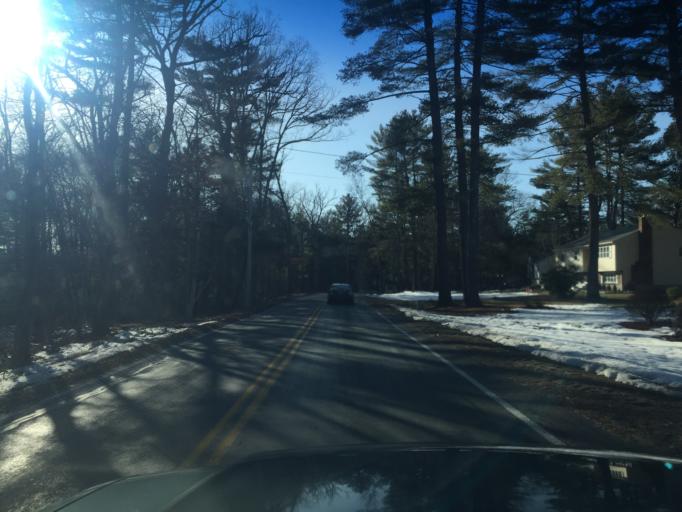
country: US
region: Massachusetts
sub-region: Norfolk County
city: Bellingham
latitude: 42.0894
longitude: -71.5075
